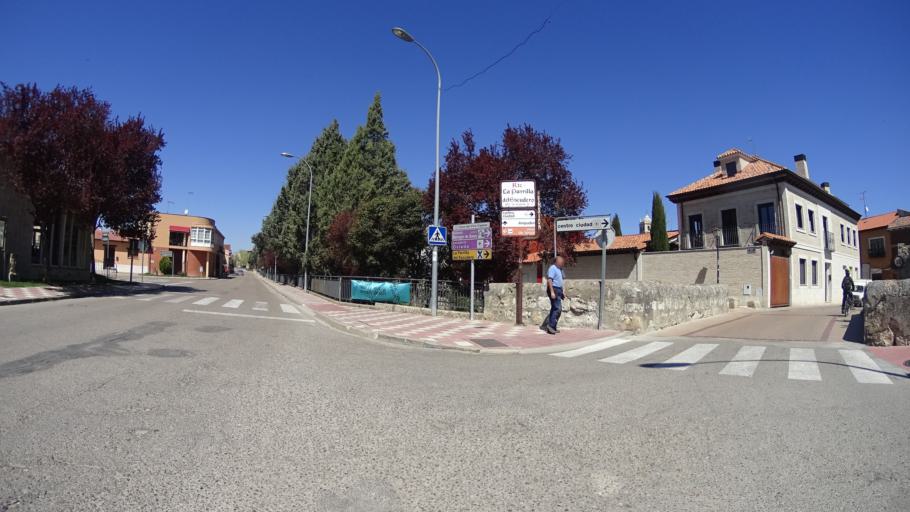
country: ES
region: Castille and Leon
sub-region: Provincia de Palencia
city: Duenas
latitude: 41.8751
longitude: -4.5456
